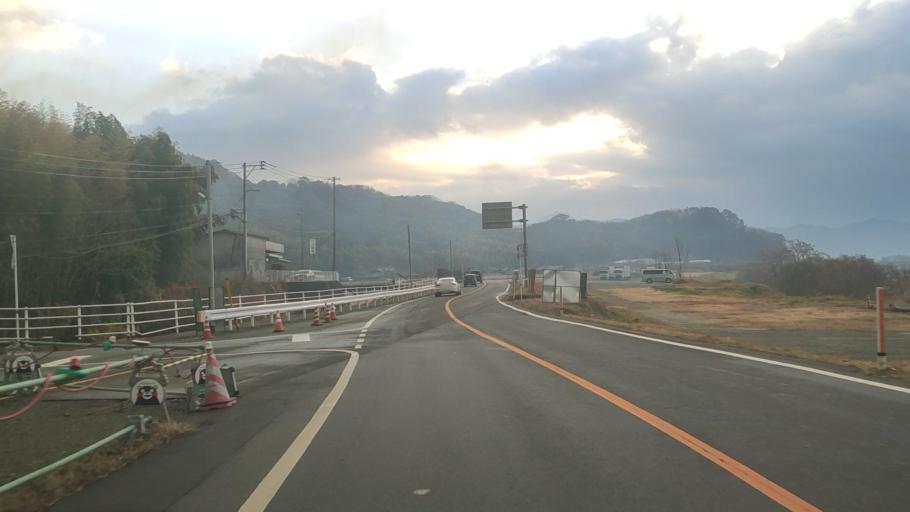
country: JP
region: Kumamoto
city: Uto
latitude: 32.7014
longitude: 130.7805
